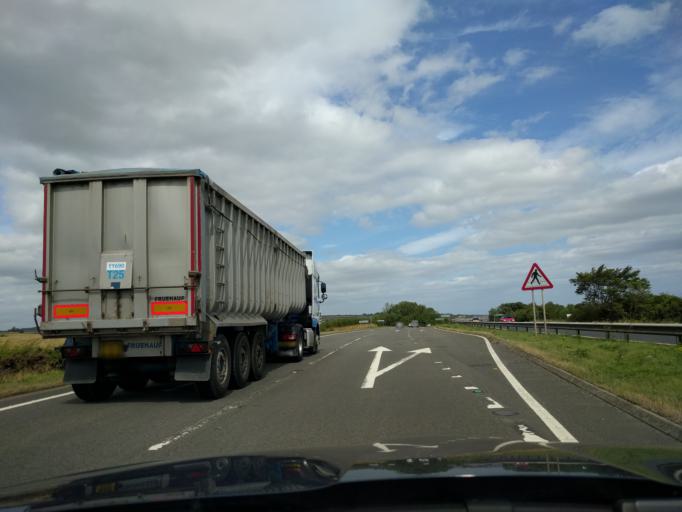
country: GB
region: England
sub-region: Northumberland
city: Alnwick
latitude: 55.3707
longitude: -1.7244
